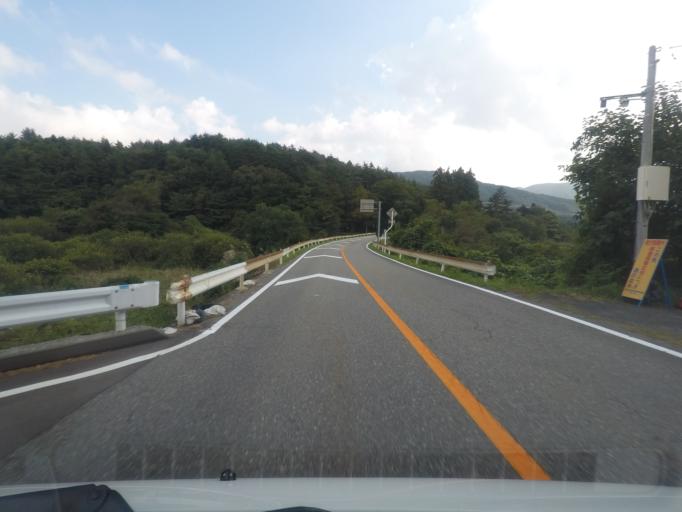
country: JP
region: Fukushima
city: Funehikimachi-funehiki
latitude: 37.5655
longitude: 140.7437
